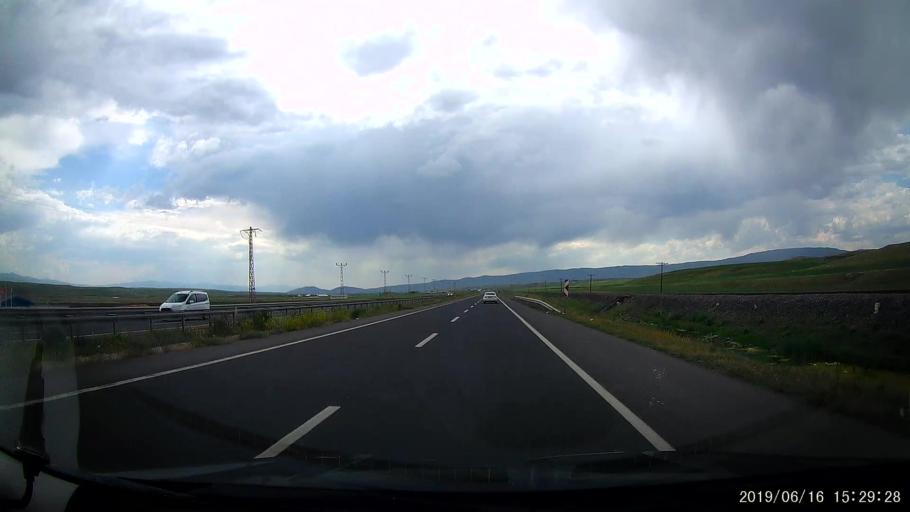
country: TR
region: Erzurum
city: Horasan
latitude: 40.0320
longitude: 42.1311
